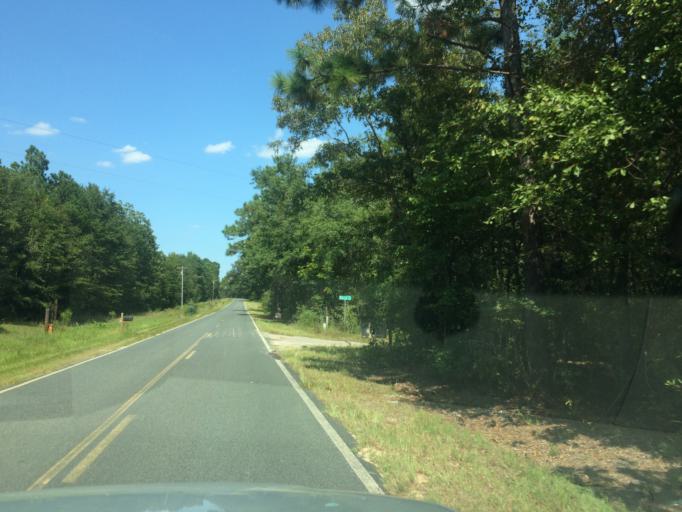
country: US
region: South Carolina
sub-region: Barnwell County
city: Williston
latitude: 33.6305
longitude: -81.4456
